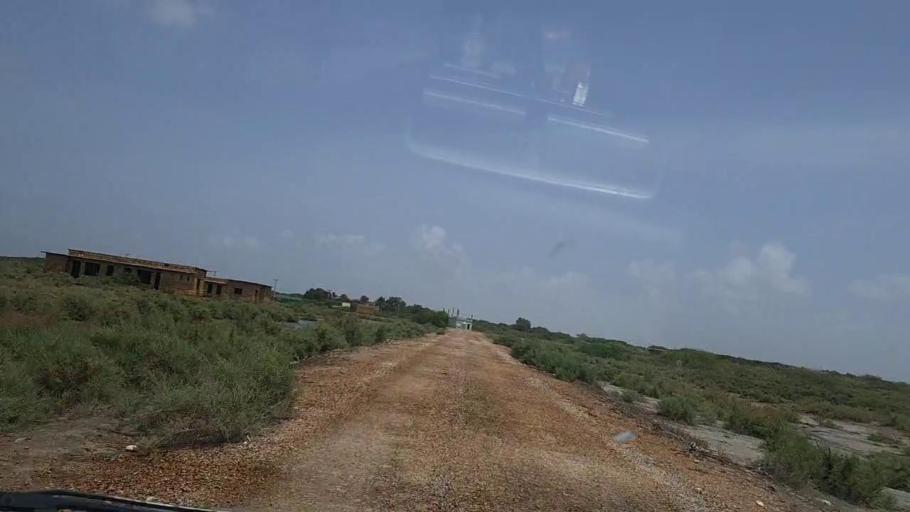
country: PK
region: Sindh
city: Keti Bandar
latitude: 24.1518
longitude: 67.5325
